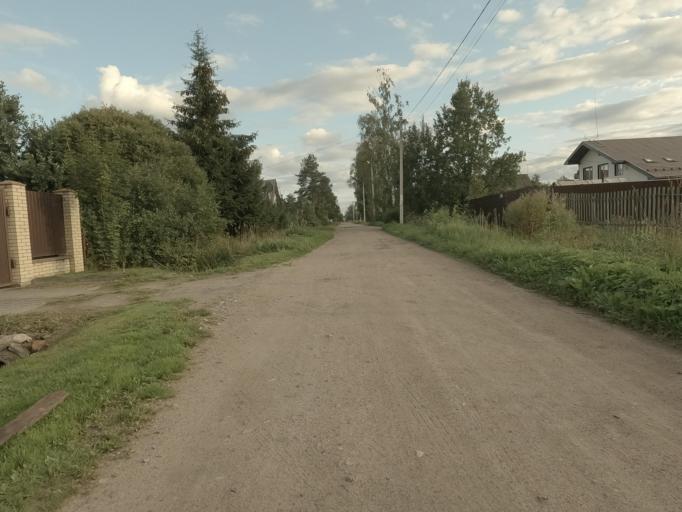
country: RU
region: Leningrad
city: Mga
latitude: 59.7619
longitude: 31.0742
